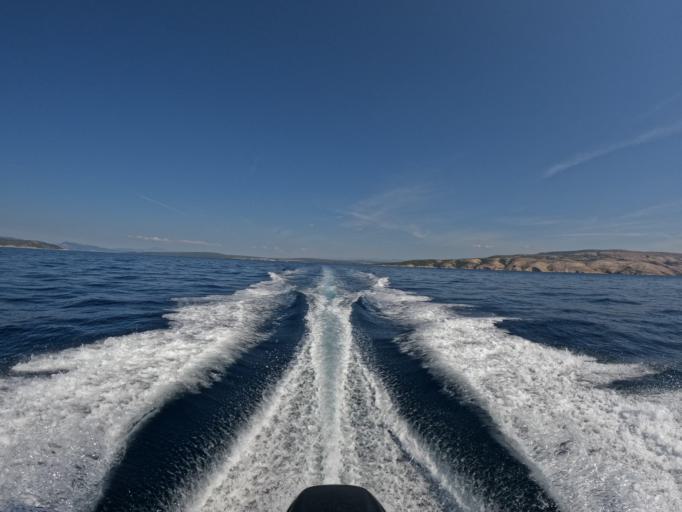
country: HR
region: Primorsko-Goranska
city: Punat
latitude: 44.9424
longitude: 14.6155
